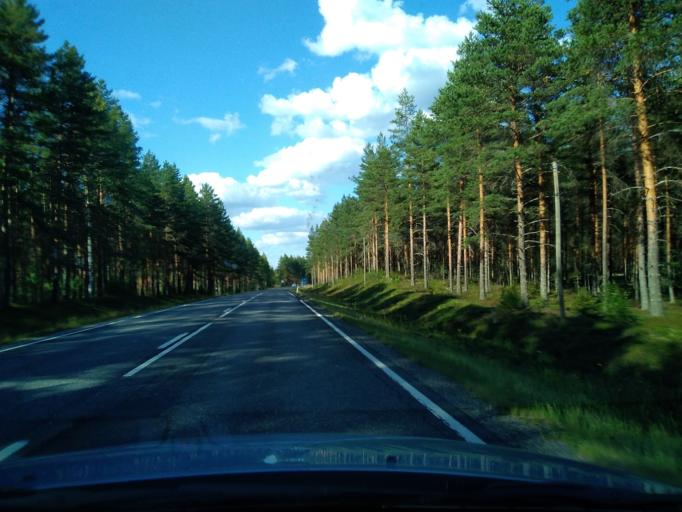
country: FI
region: Pirkanmaa
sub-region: Ylae-Pirkanmaa
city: Vilppula
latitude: 61.9439
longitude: 24.5418
